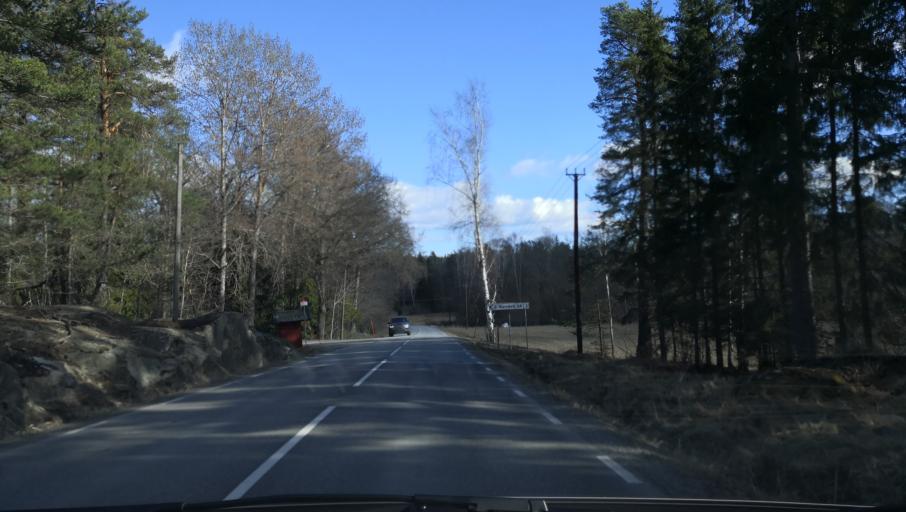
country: SE
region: Stockholm
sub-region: Varmdo Kommun
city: Hemmesta
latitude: 59.3605
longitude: 18.5393
